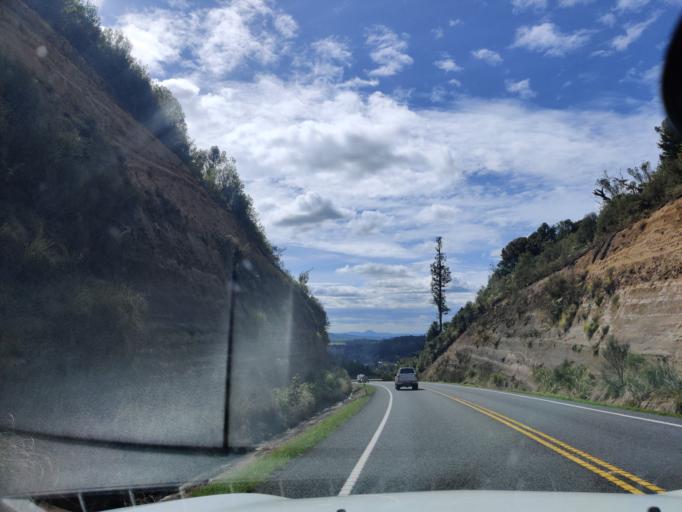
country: NZ
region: Waikato
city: Turangi
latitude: -39.1344
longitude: 175.3987
